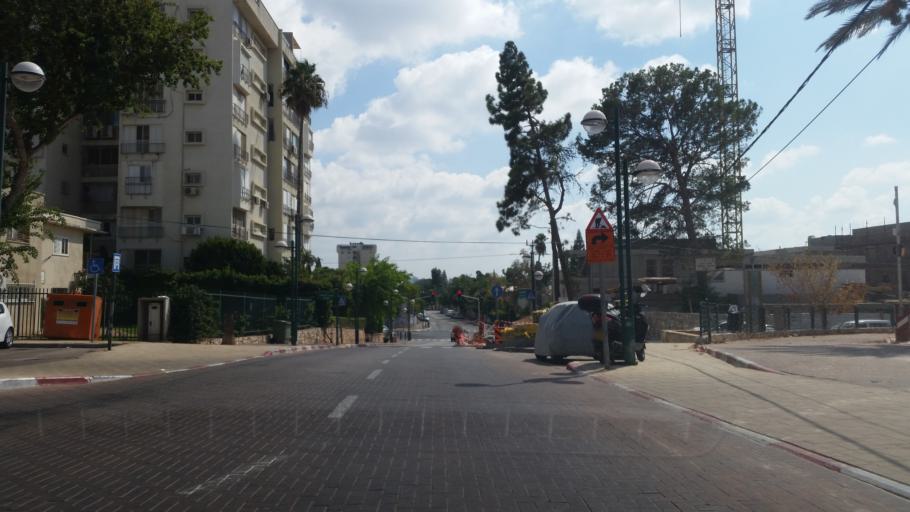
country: IL
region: Tel Aviv
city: Ramat HaSharon
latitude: 32.1384
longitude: 34.8386
